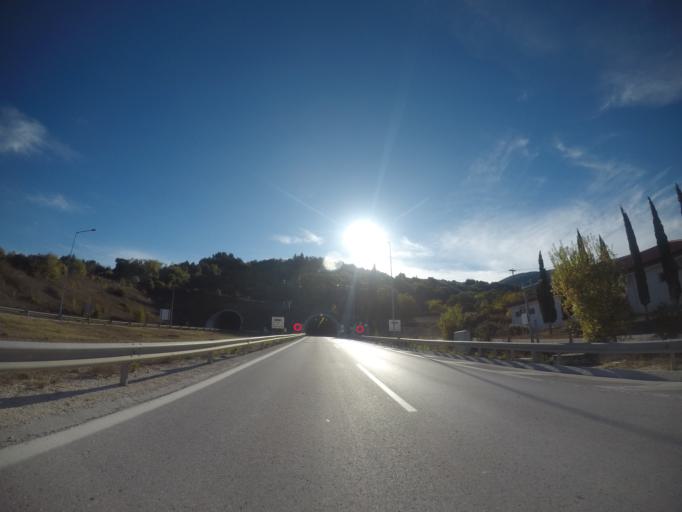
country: GR
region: Epirus
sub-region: Nomos Ioanninon
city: Pedini
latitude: 39.5866
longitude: 20.8139
